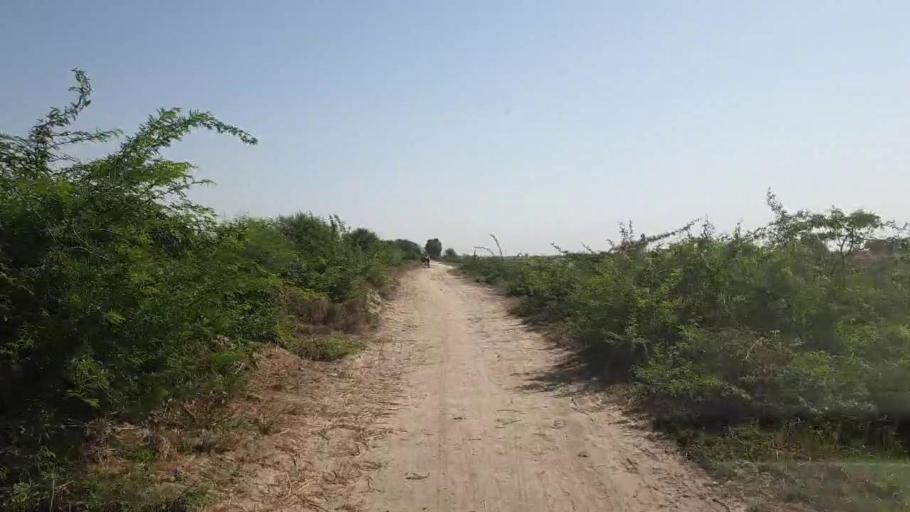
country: PK
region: Sindh
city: Kadhan
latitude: 24.6118
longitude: 68.9989
